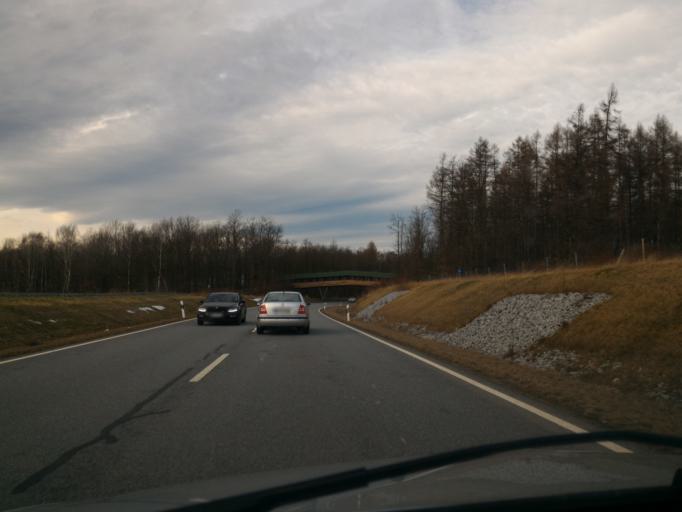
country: DE
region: Saxony
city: Bischofswerda
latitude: 51.1089
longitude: 14.1833
